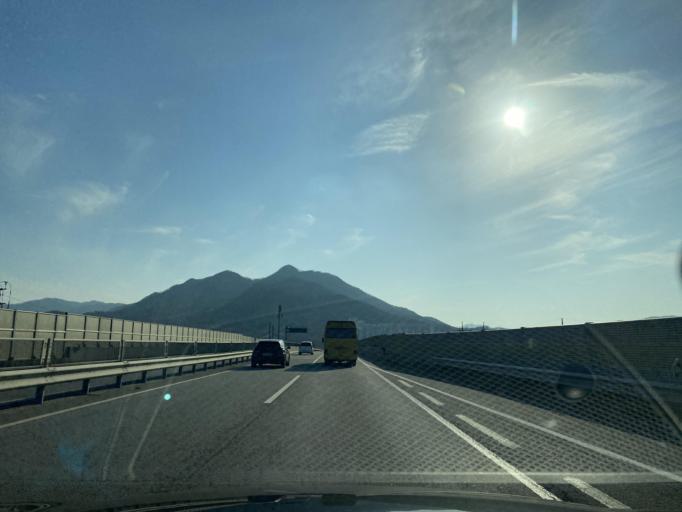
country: KR
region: Chungcheongnam-do
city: Asan
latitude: 36.7641
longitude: 127.0367
